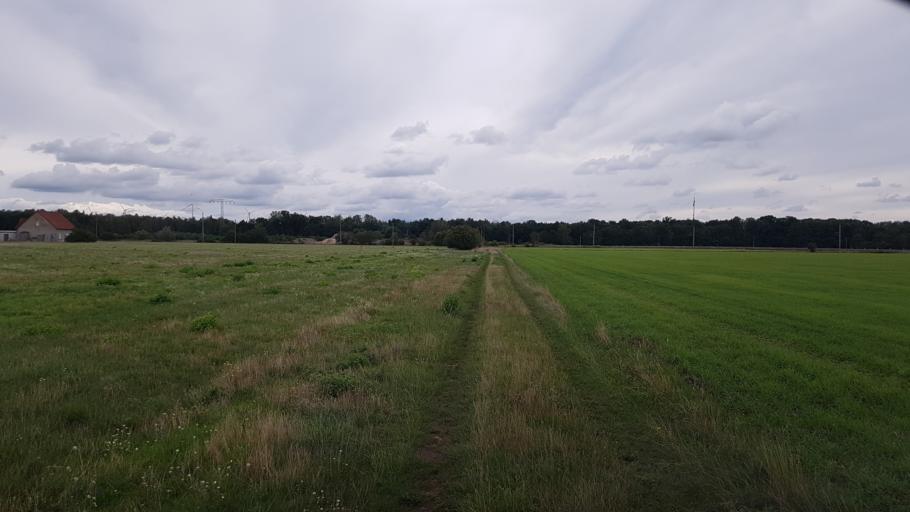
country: DE
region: Brandenburg
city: Doberlug-Kirchhain
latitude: 51.6385
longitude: 13.5838
